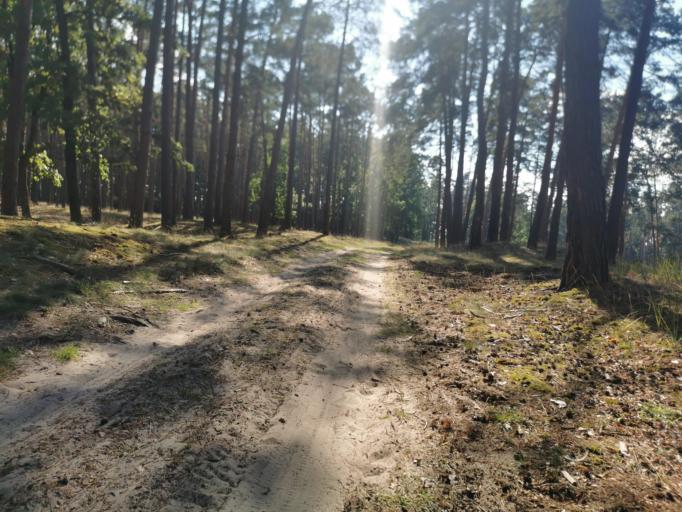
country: SK
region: Trnavsky
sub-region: Okres Senica
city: Senica
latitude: 48.6024
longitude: 17.2628
